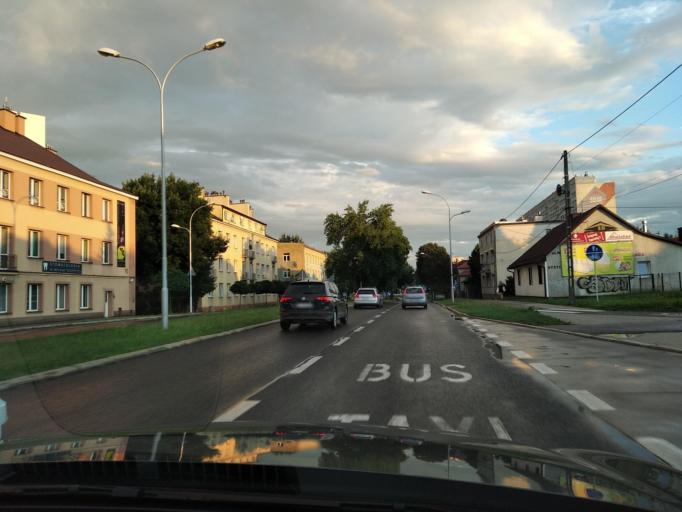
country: PL
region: Subcarpathian Voivodeship
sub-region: Rzeszow
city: Rzeszow
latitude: 50.0502
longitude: 21.9979
